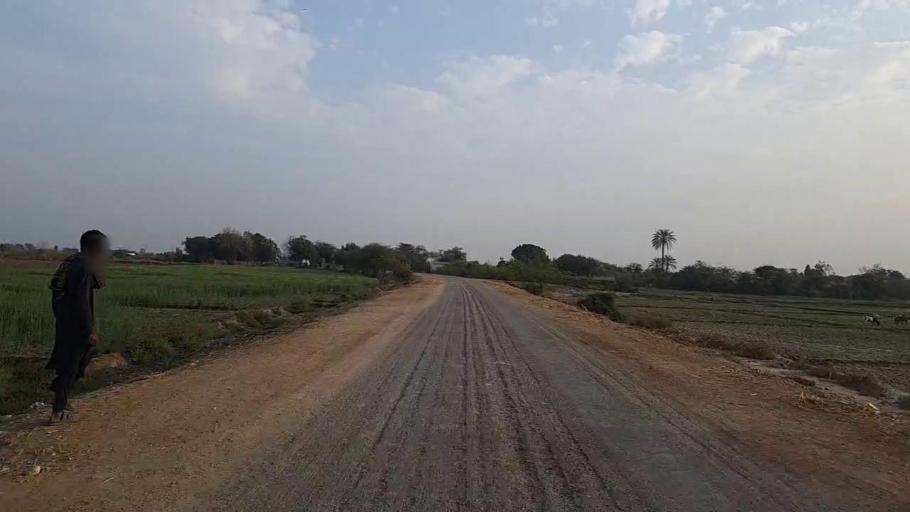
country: PK
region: Sindh
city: Samaro
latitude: 25.3912
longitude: 69.3240
